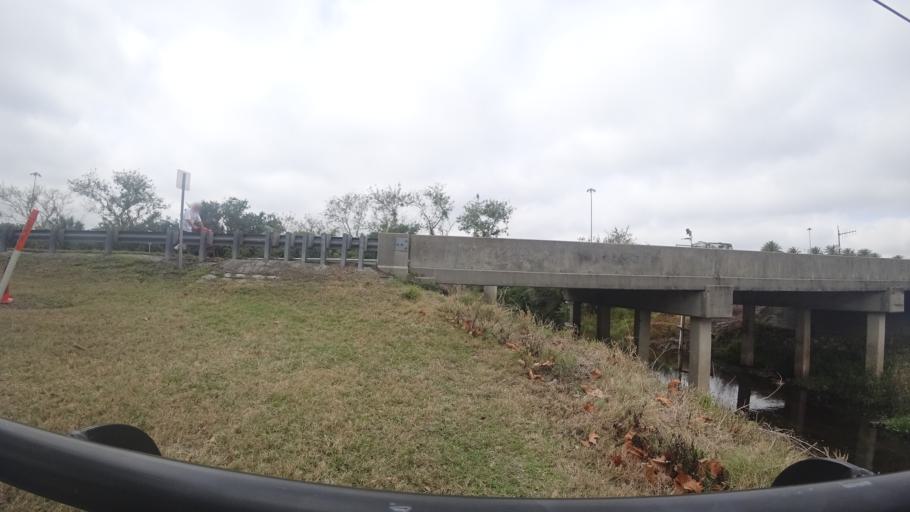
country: US
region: Florida
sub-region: Manatee County
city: Ellenton
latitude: 27.5797
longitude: -82.5133
